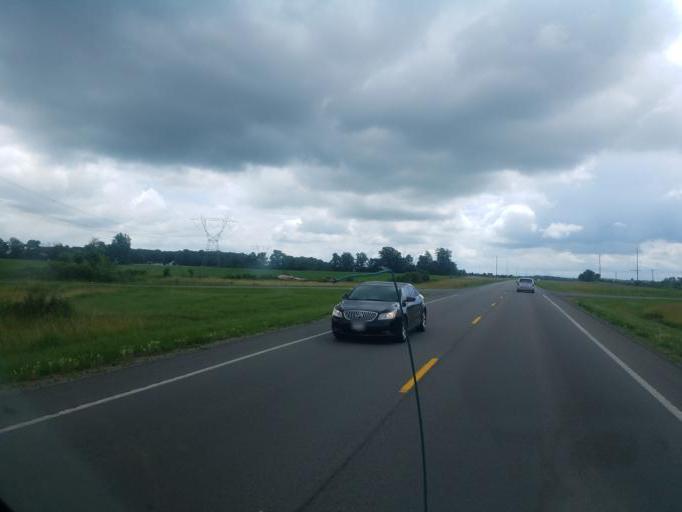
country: US
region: Ohio
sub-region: Logan County
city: Russells Point
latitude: 40.4504
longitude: -83.8324
